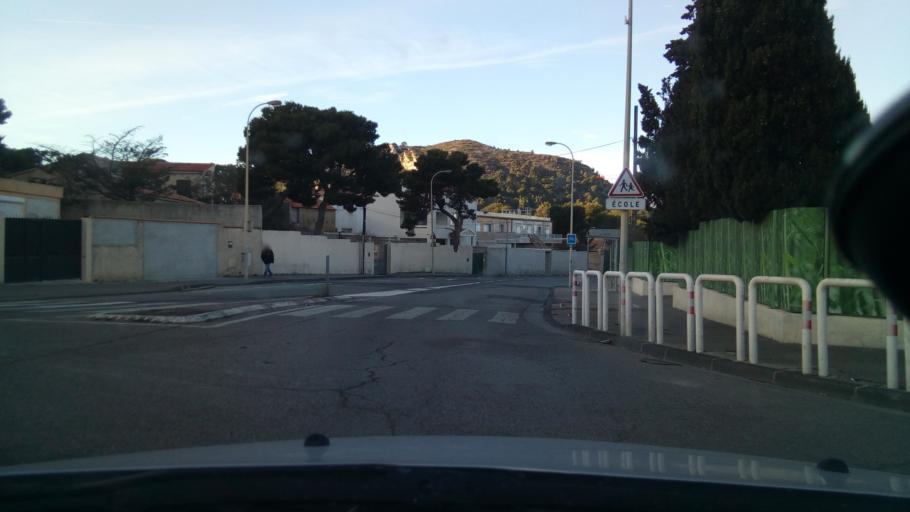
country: FR
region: Provence-Alpes-Cote d'Azur
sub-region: Departement des Bouches-du-Rhone
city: Marseille 09
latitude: 43.2291
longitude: 5.4020
